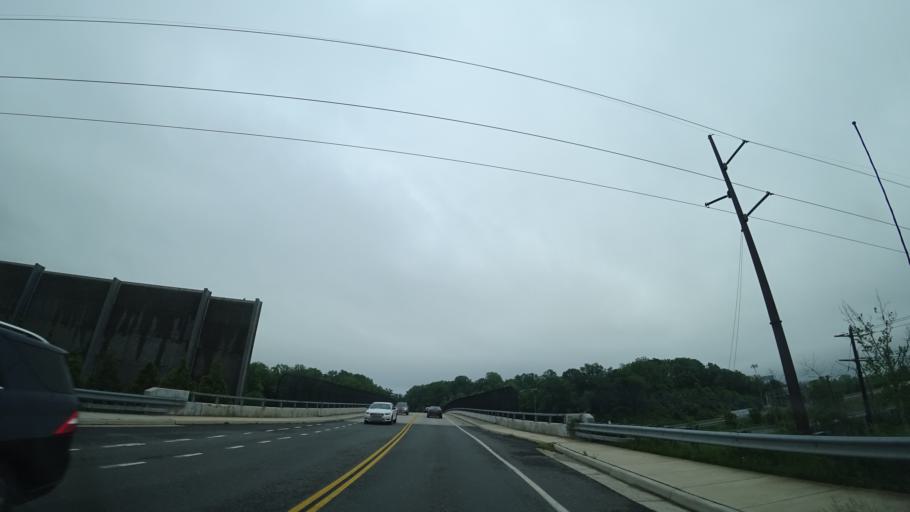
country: US
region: Virginia
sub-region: Fairfax County
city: Pimmit Hills
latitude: 38.9366
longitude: -77.2093
